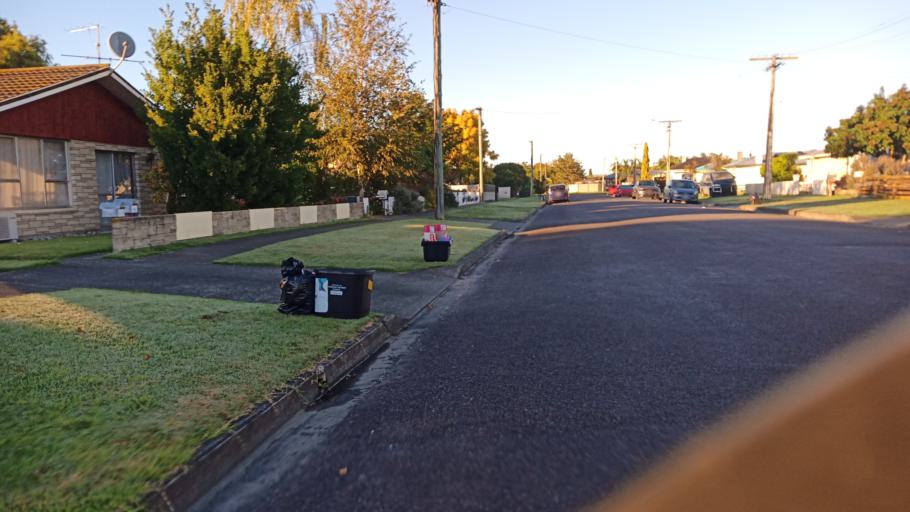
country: NZ
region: Gisborne
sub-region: Gisborne District
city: Gisborne
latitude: -38.6512
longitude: 177.9931
